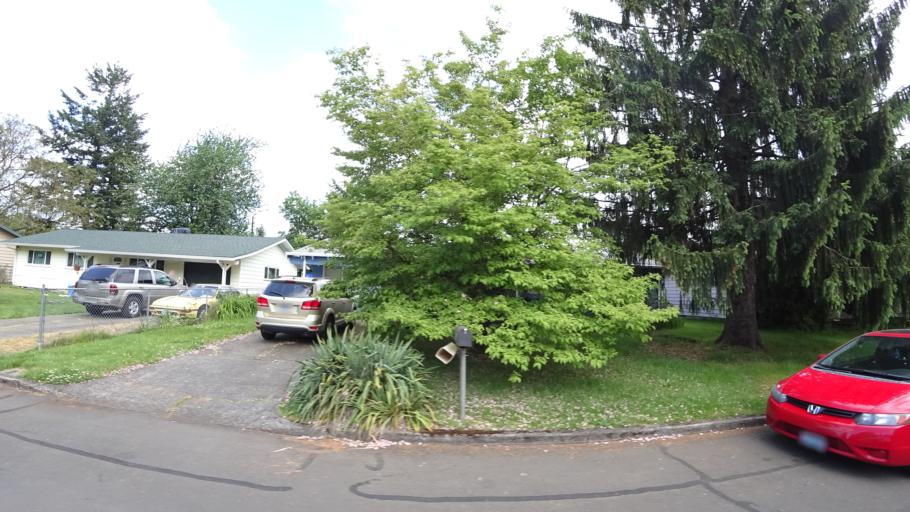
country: US
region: Oregon
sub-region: Multnomah County
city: Fairview
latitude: 45.5162
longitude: -122.4777
